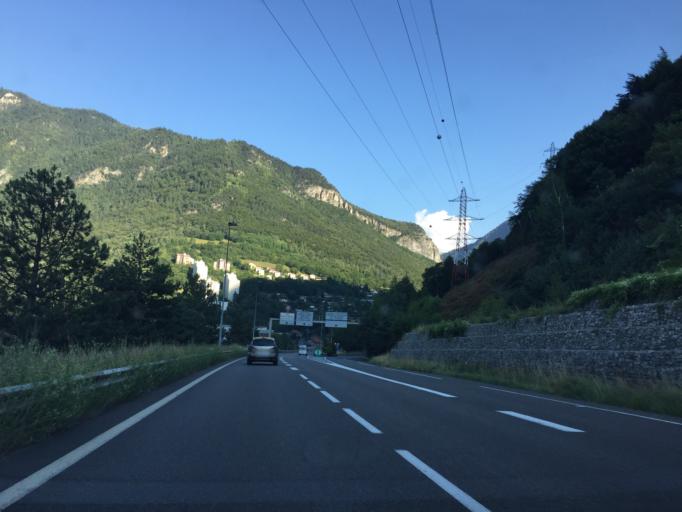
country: FR
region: Rhone-Alpes
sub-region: Departement de la Savoie
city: Moutiers
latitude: 45.4859
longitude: 6.5224
